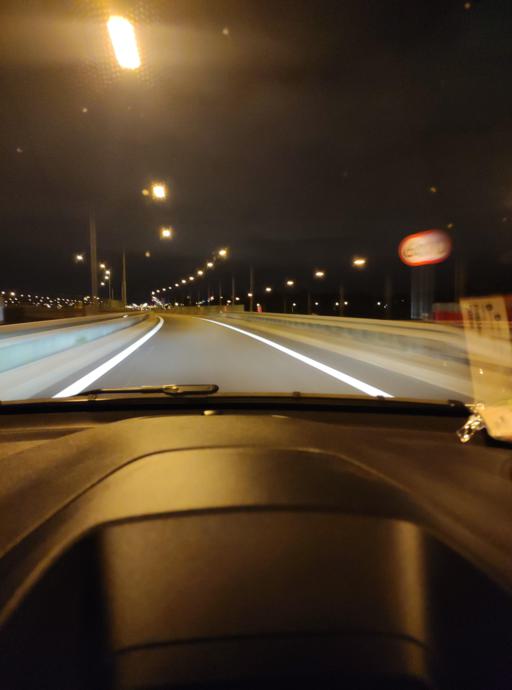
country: PL
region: Masovian Voivodeship
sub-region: Powiat piaseczynski
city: Mysiadlo
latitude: 52.1364
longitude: 20.9895
